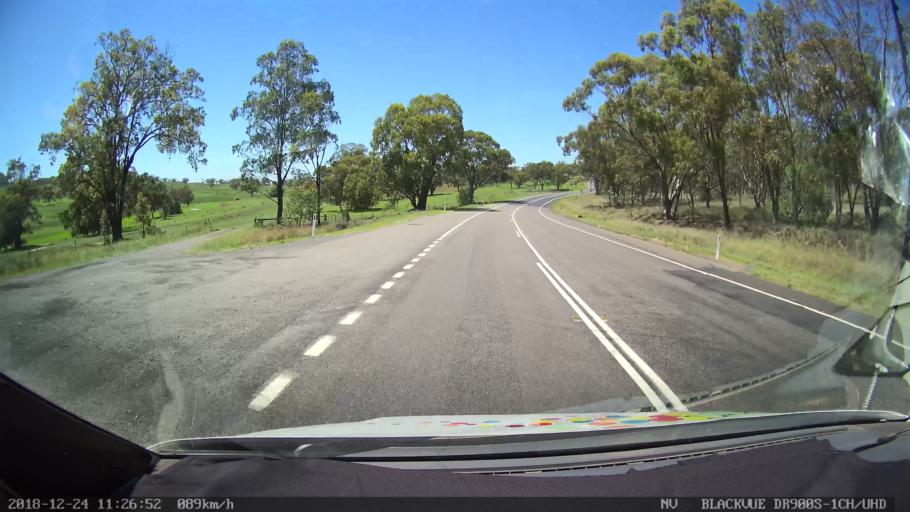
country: AU
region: New South Wales
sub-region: Upper Hunter Shire
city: Merriwa
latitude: -32.1745
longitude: 150.4336
